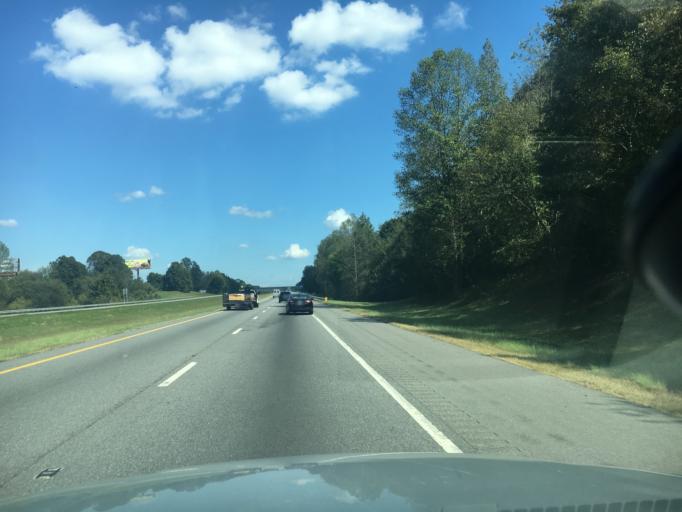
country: US
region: North Carolina
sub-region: Catawba County
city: Conover
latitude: 35.7101
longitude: -81.2381
